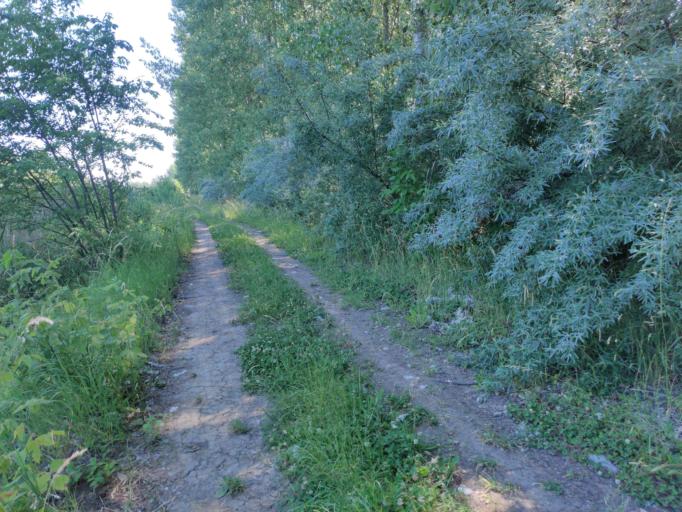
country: HU
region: Hajdu-Bihar
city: Balmazujvaros
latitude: 47.5865
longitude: 21.3607
